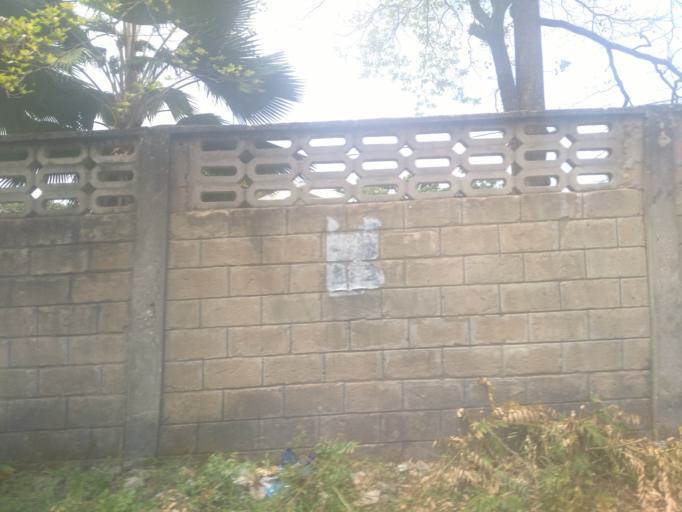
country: TZ
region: Zanzibar Urban/West
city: Zanzibar
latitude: -6.2319
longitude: 39.2122
